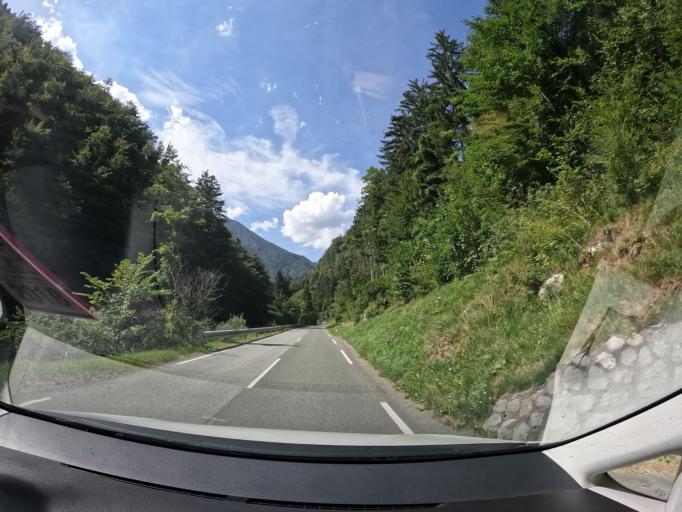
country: SI
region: Jezersko
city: Zgornje Jezersko
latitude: 46.3582
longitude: 14.4629
